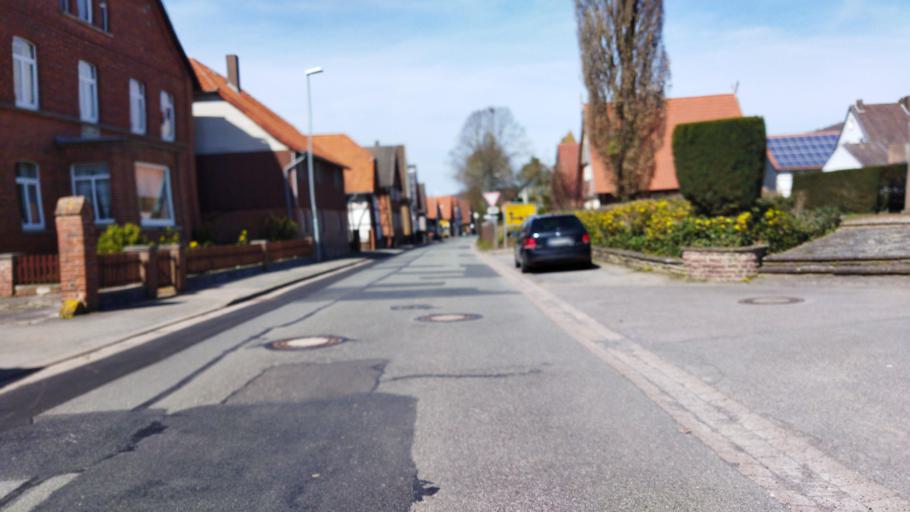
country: DE
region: Lower Saxony
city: Hehlen
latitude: 52.0321
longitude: 9.4313
